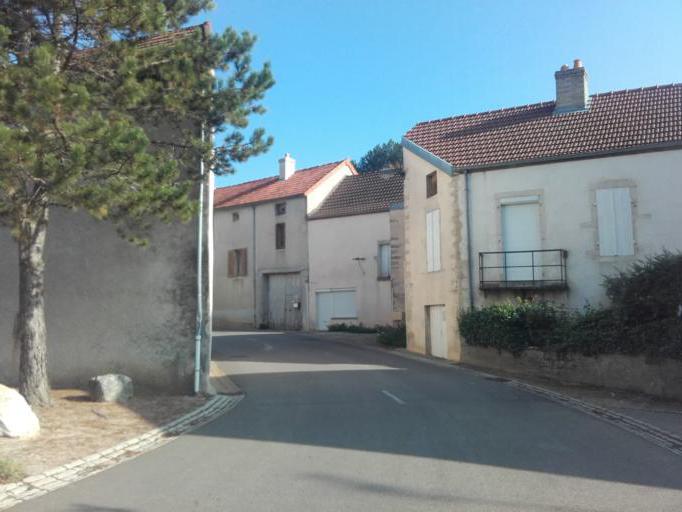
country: FR
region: Bourgogne
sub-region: Departement de la Cote-d'Or
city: Savigny-les-Beaune
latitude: 47.1053
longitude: 4.8766
